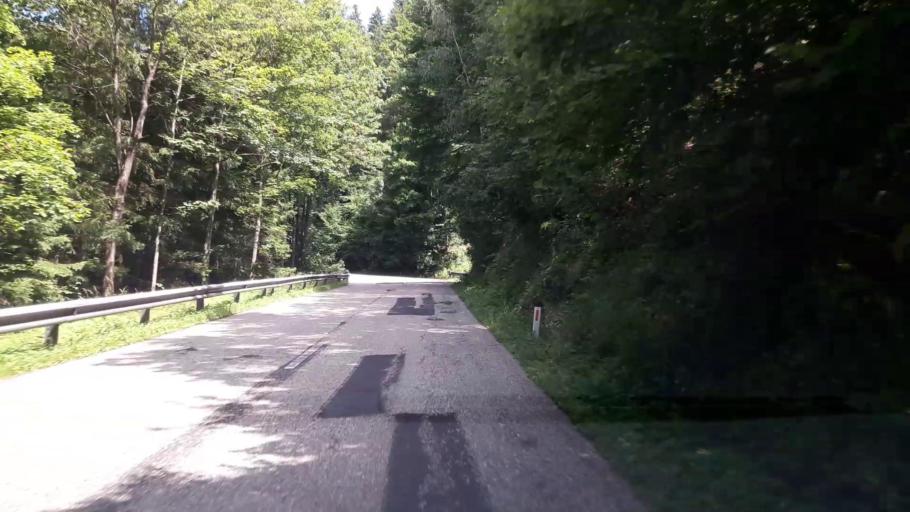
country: AT
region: Upper Austria
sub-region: Politischer Bezirk Rohrbach
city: Atzesberg
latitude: 48.4776
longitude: 13.9312
